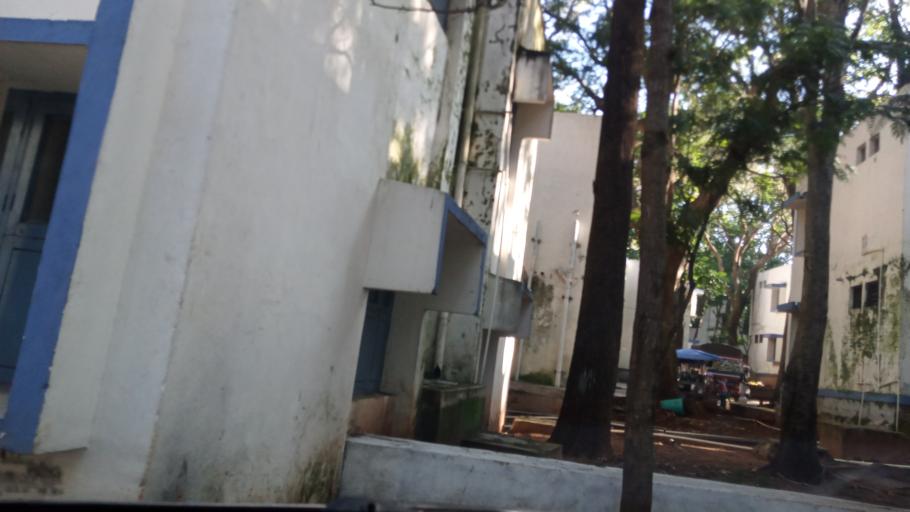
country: IN
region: Andhra Pradesh
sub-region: Chittoor
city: Tirumala
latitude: 13.6720
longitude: 79.3489
